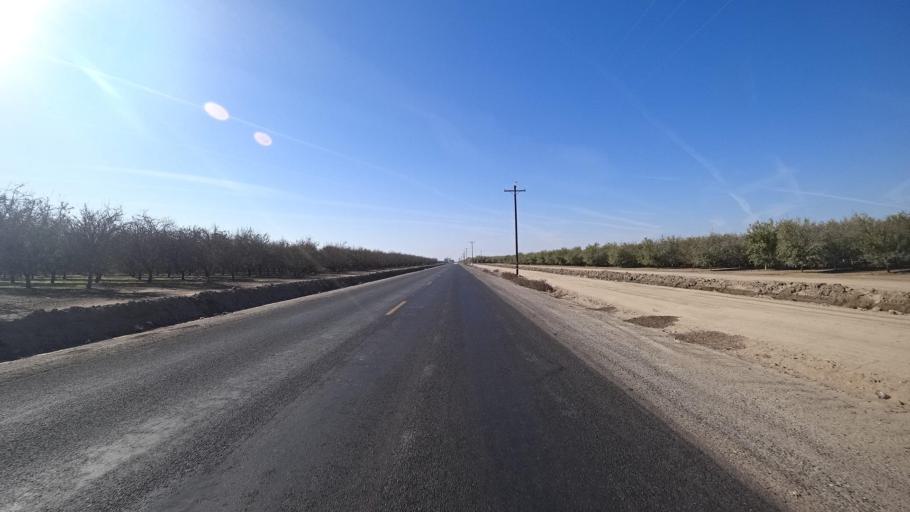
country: US
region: California
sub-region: Kern County
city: Wasco
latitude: 35.6452
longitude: -119.3087
